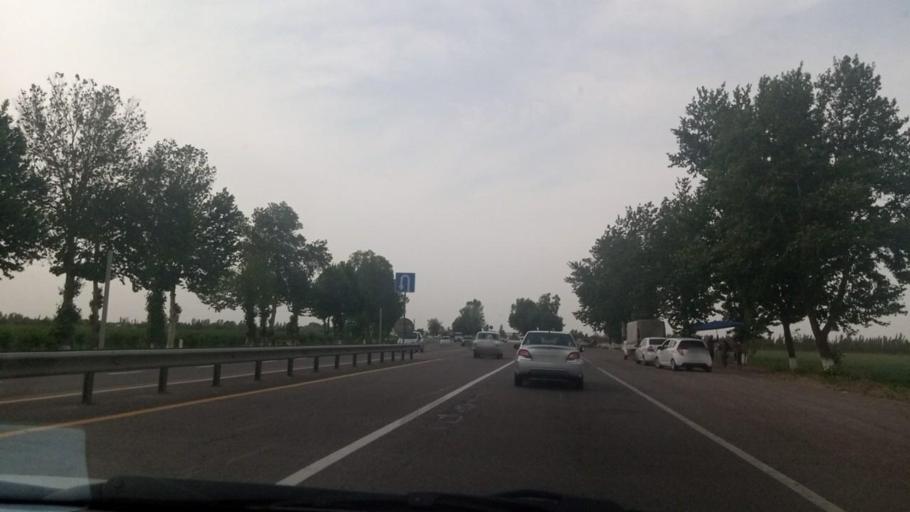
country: UZ
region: Toshkent Shahri
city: Bektemir
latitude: 41.1422
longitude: 69.4327
